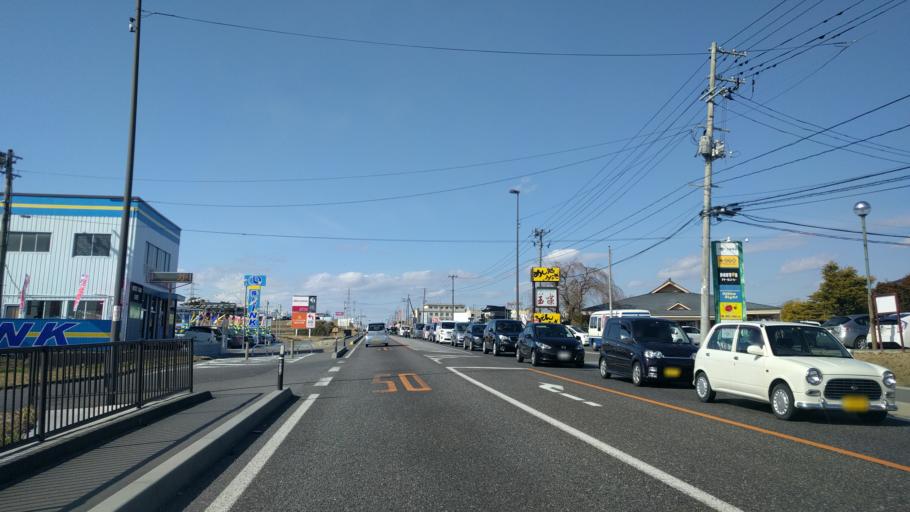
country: JP
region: Fukushima
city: Koriyama
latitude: 37.4321
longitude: 140.3816
